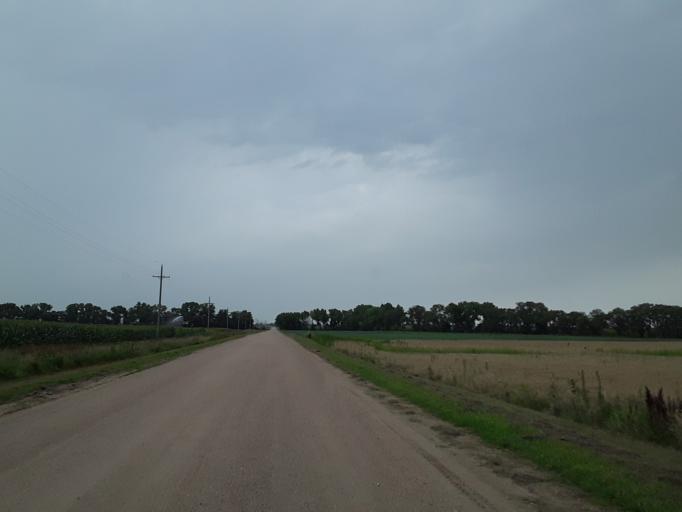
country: US
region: Nebraska
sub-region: Saunders County
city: Yutan
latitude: 41.1615
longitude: -96.4449
